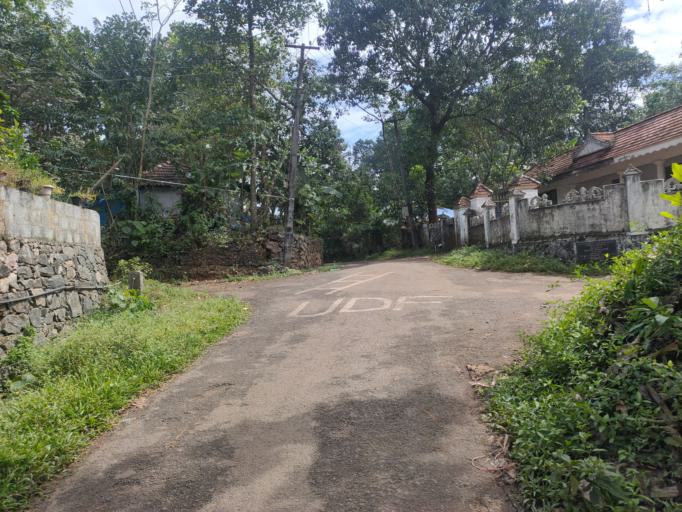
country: IN
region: Kerala
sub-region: Ernakulam
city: Kotamangalam
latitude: 10.0053
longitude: 76.6420
